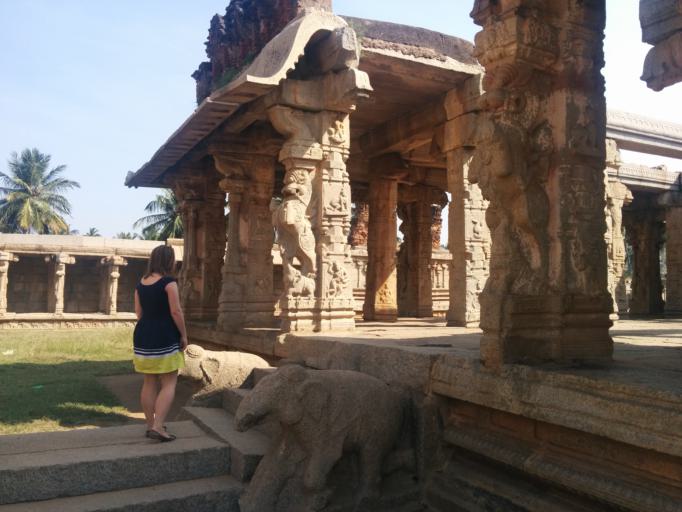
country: IN
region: Karnataka
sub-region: Bellary
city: Hampi
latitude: 15.3322
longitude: 76.4700
